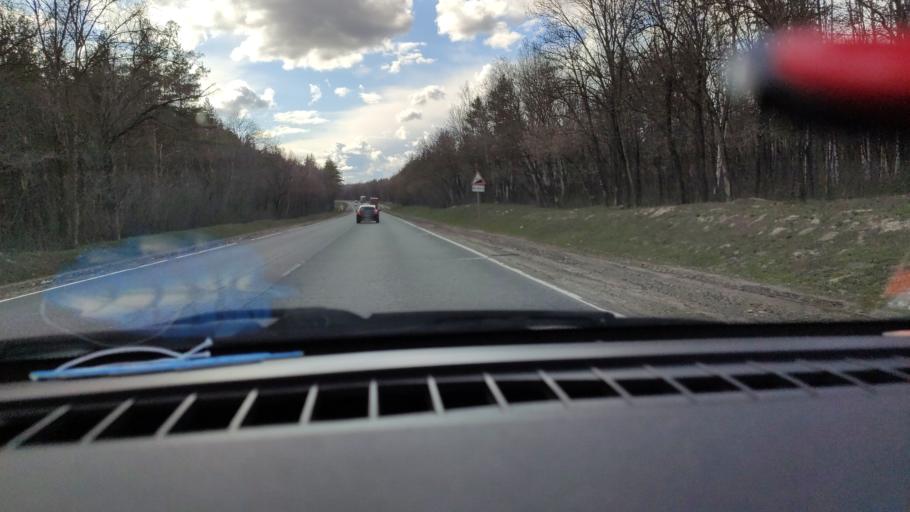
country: RU
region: Saratov
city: Vol'sk
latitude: 52.1063
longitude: 47.4290
